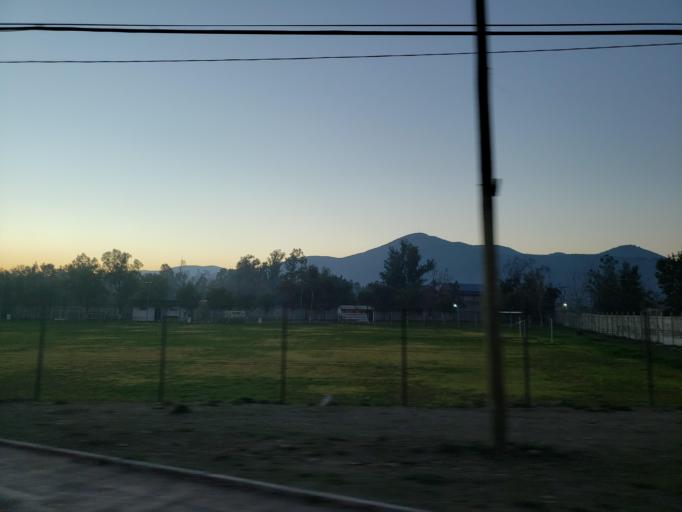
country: CL
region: Santiago Metropolitan
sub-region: Provincia de Talagante
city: Talagante
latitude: -33.6735
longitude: -70.9483
